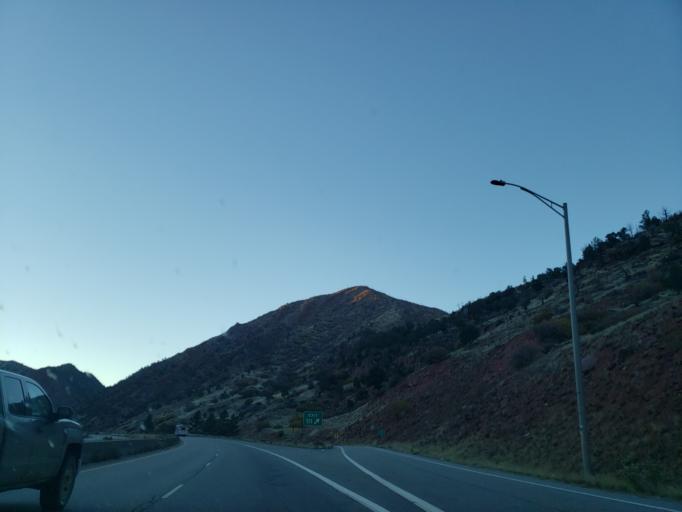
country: US
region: Colorado
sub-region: Garfield County
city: Glenwood Springs
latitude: 39.5638
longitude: -107.4090
